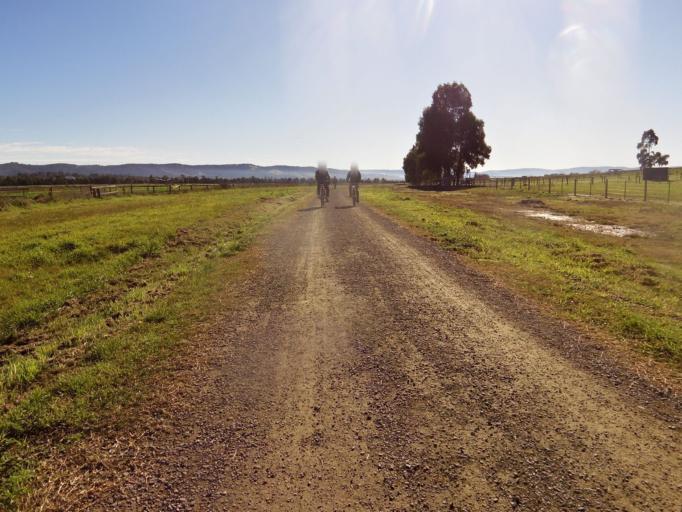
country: AU
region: Victoria
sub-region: Yarra Ranges
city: Lilydale
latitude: -37.7162
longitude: 145.3678
